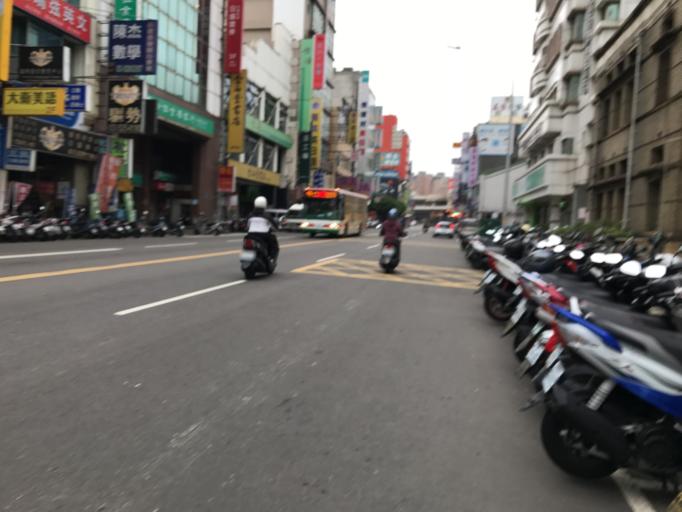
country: TW
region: Taiwan
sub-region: Hsinchu
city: Hsinchu
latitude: 24.8041
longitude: 120.9723
